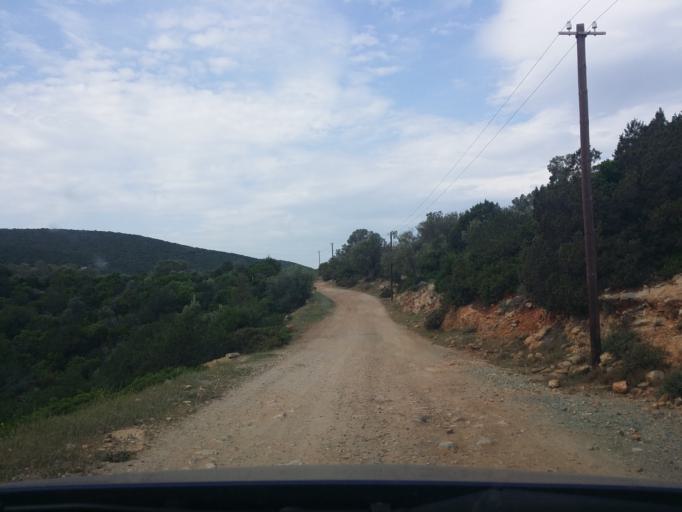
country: GR
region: Attica
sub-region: Nomos Piraios
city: Poros
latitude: 37.5371
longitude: 23.4807
